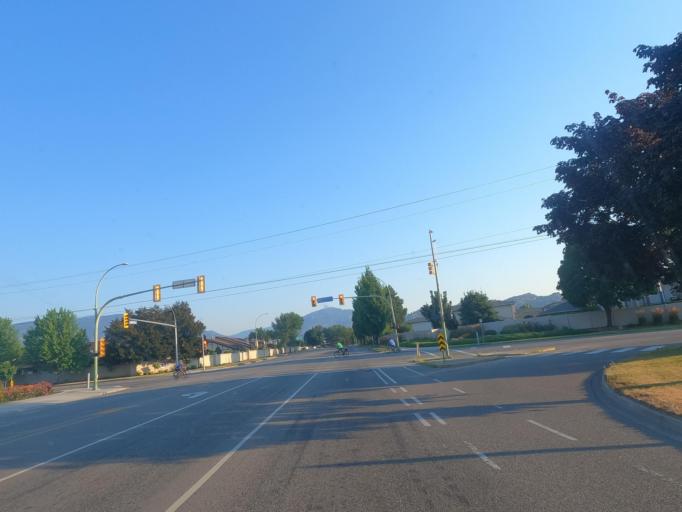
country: CA
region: British Columbia
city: Kelowna
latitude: 49.8724
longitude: -119.4758
